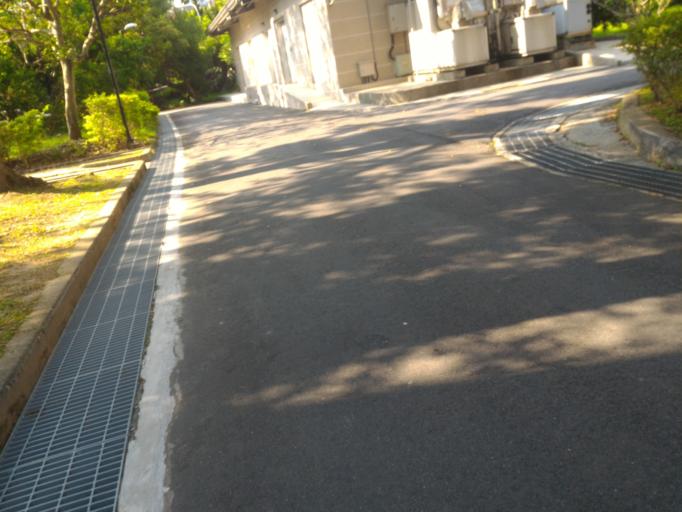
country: TW
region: Taipei
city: Taipei
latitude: 25.0422
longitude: 121.6149
